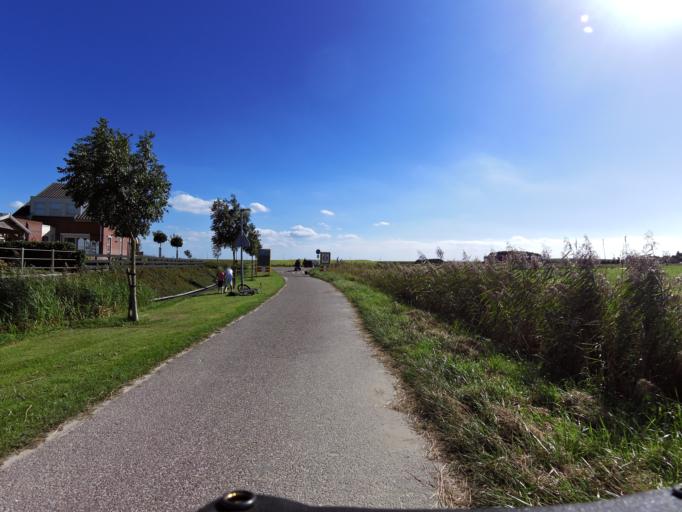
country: NL
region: South Holland
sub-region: Gemeente Goeree-Overflakkee
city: Ouddorp
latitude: 51.8041
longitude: 3.9411
